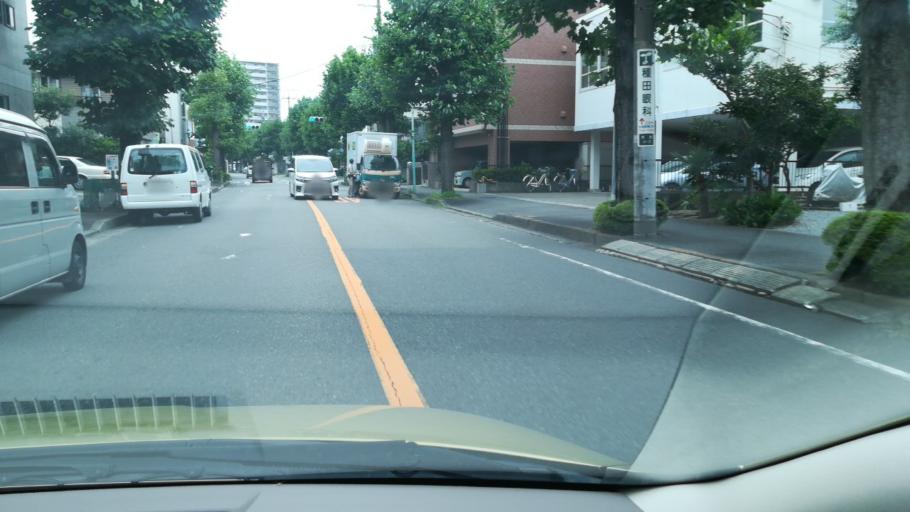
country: JP
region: Tokyo
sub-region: Machida-shi
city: Machida
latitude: 35.5705
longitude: 139.3880
